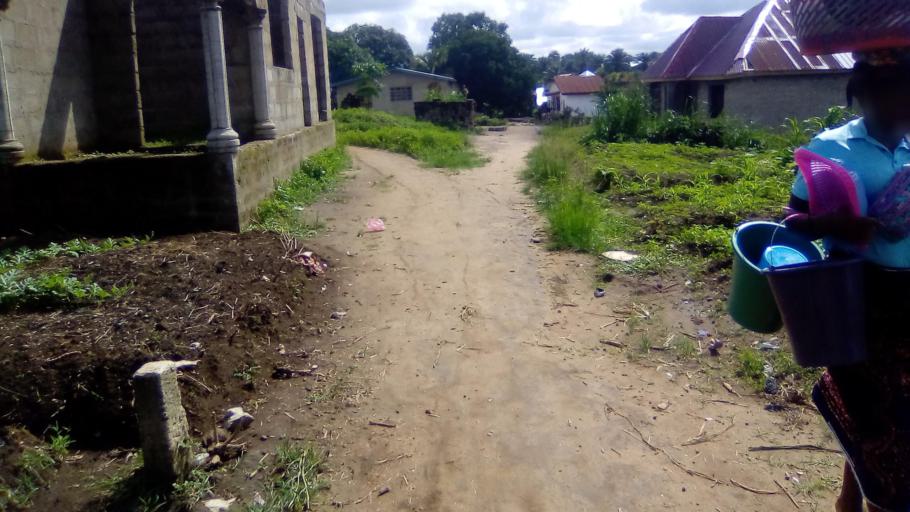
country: SL
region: Southern Province
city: Bo
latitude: 7.9771
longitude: -11.7250
